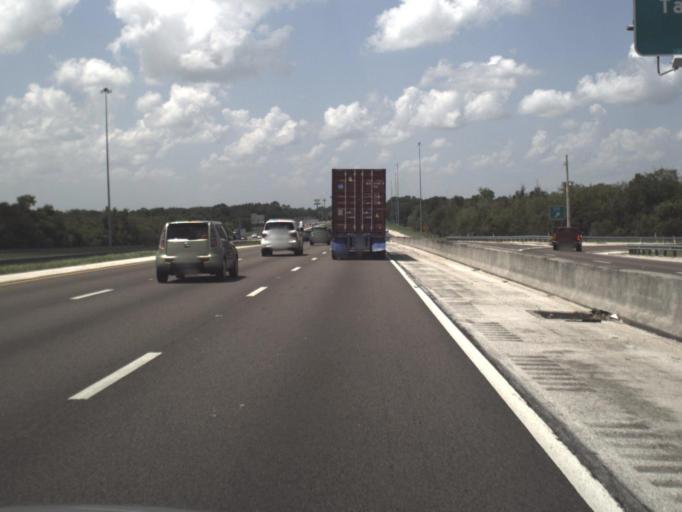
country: US
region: Florida
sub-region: Hillsborough County
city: Plant City
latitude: 28.0318
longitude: -82.1358
